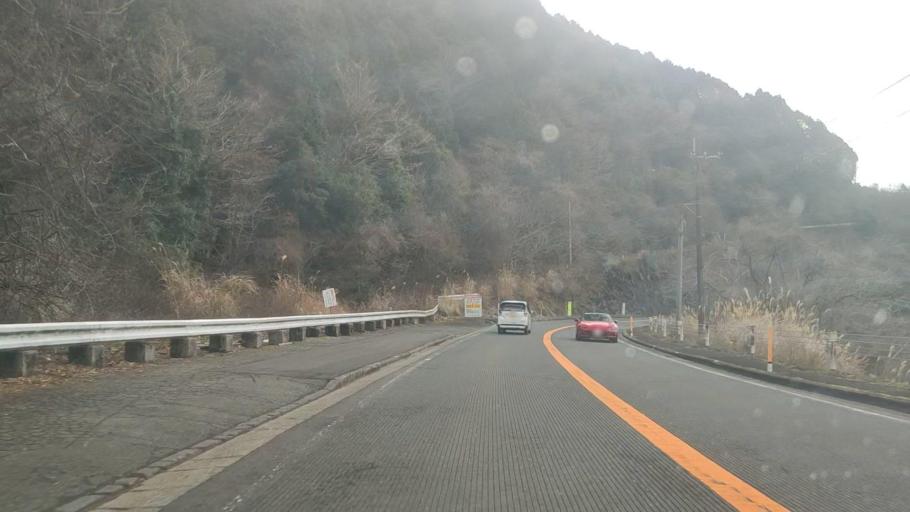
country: JP
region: Kumamoto
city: Hitoyoshi
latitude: 32.0831
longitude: 130.8009
